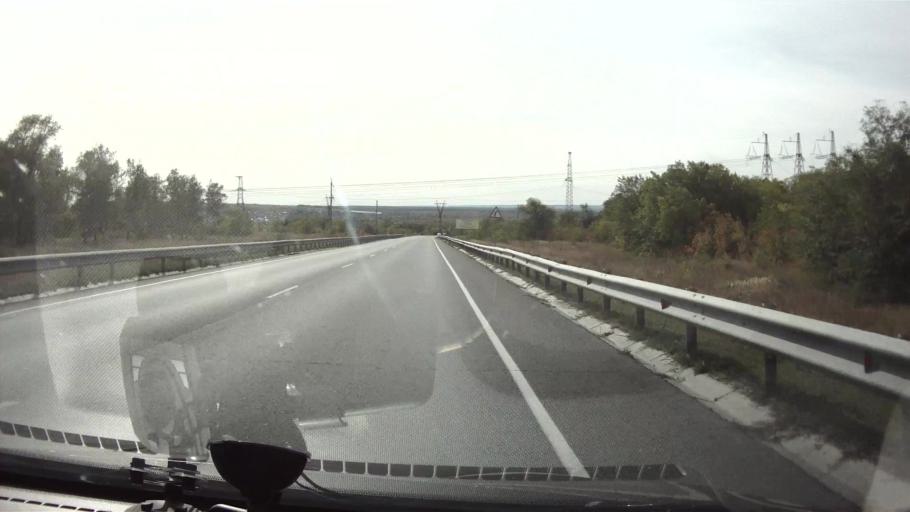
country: RU
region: Saratov
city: Balakovo
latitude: 52.0857
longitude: 47.6791
